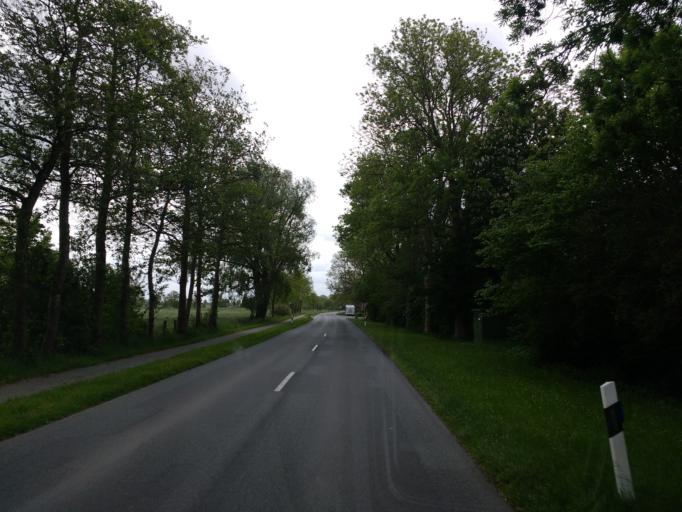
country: DE
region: Lower Saxony
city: Schillig
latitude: 53.6446
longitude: 7.9999
